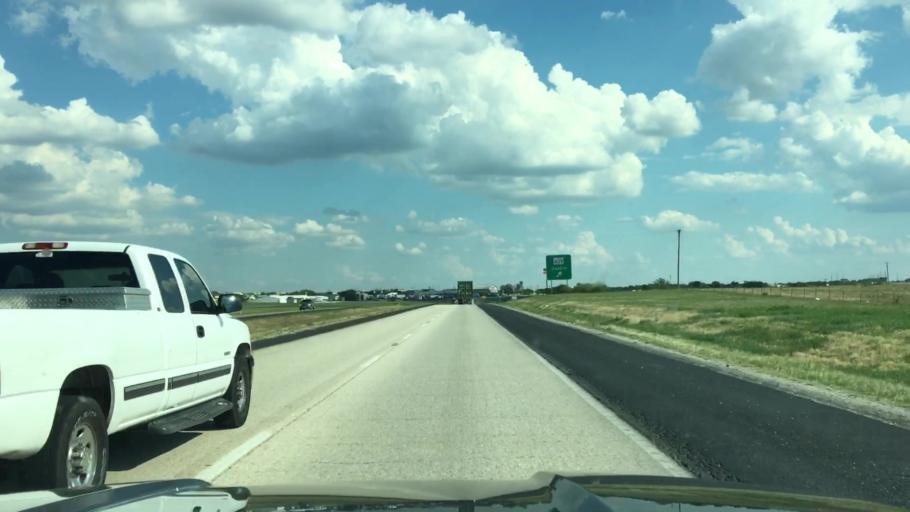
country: US
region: Texas
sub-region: Wise County
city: New Fairview
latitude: 33.1090
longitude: -97.4761
